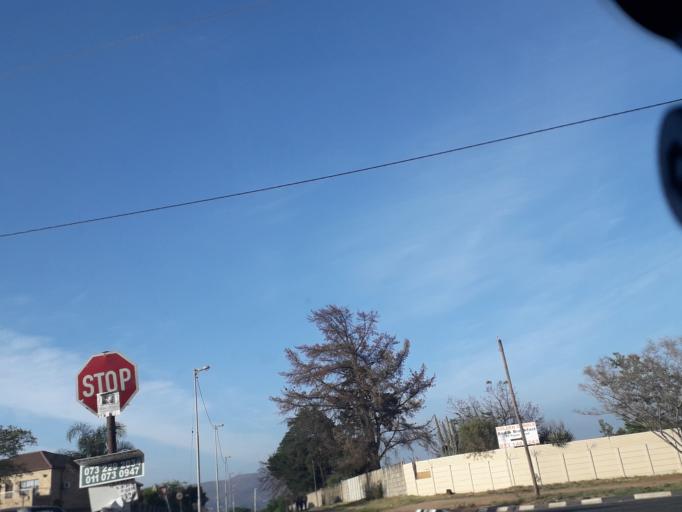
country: ZA
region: Gauteng
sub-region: City of Johannesburg Metropolitan Municipality
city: Roodepoort
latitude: -26.0923
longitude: 27.9003
